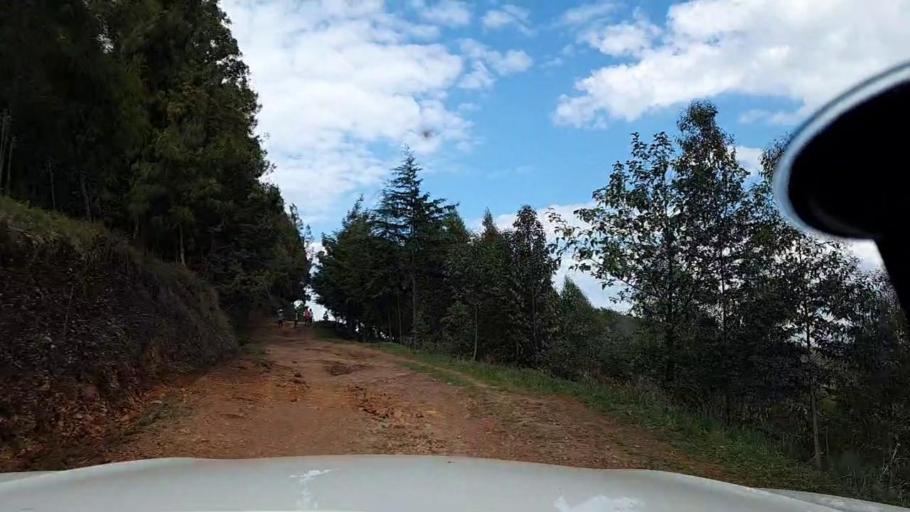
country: RW
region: Kigali
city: Kigali
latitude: -1.7882
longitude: 29.8303
